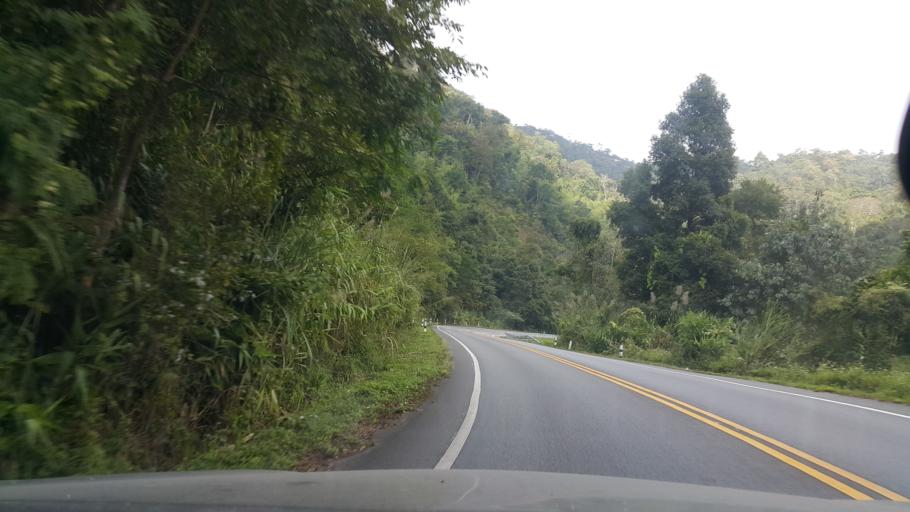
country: TH
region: Lampang
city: Wang Nuea
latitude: 19.0704
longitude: 99.7660
